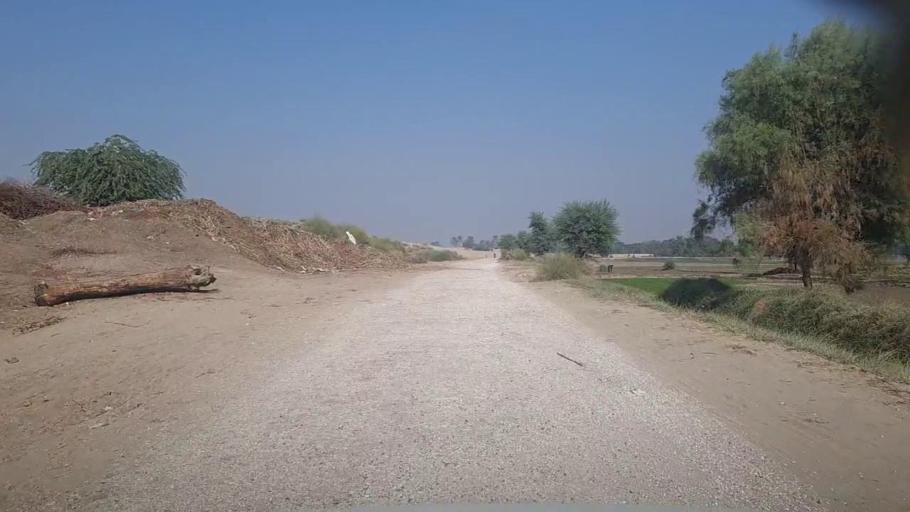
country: PK
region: Sindh
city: Kandiari
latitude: 26.9252
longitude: 68.5188
